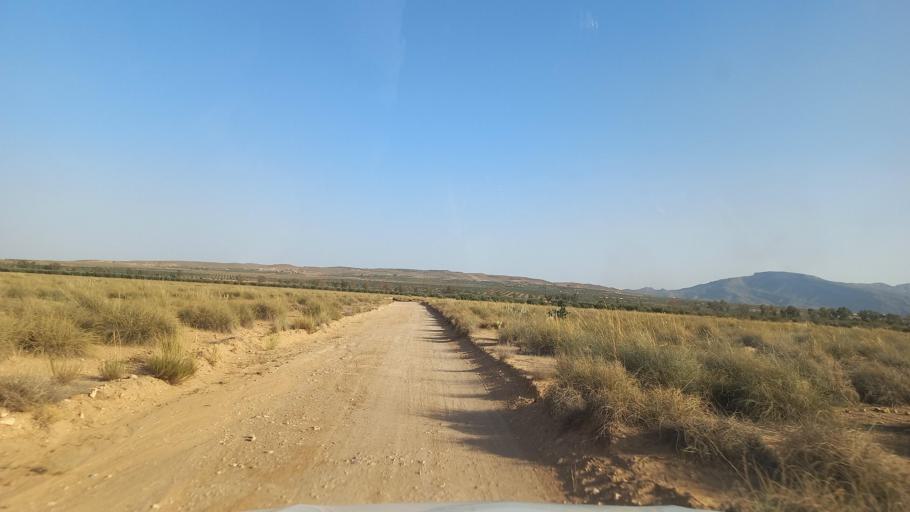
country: TN
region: Al Qasrayn
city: Kasserine
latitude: 35.2315
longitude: 8.9399
